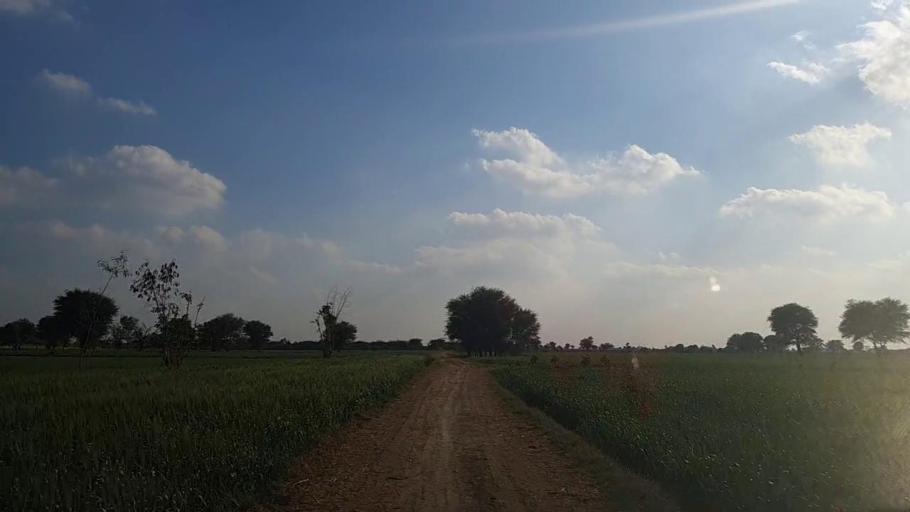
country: PK
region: Sindh
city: Tando Mittha Khan
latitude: 25.9386
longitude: 69.2108
